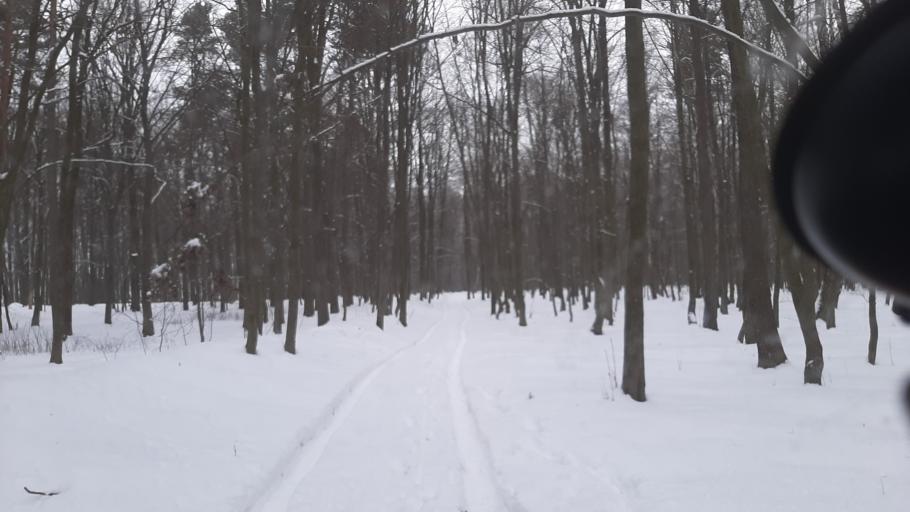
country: PL
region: Lublin Voivodeship
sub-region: Powiat lubelski
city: Garbow
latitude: 51.3708
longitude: 22.3893
